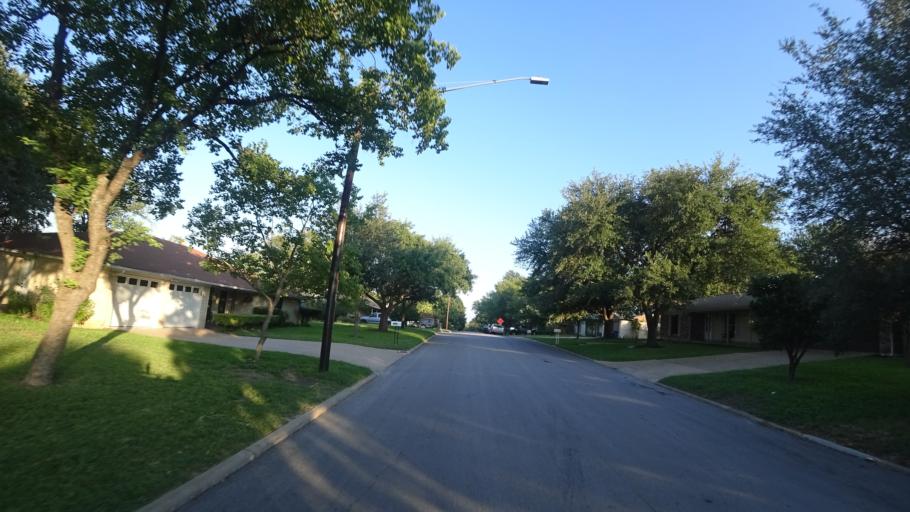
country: US
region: Texas
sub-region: Travis County
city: Wells Branch
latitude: 30.3689
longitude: -97.6793
